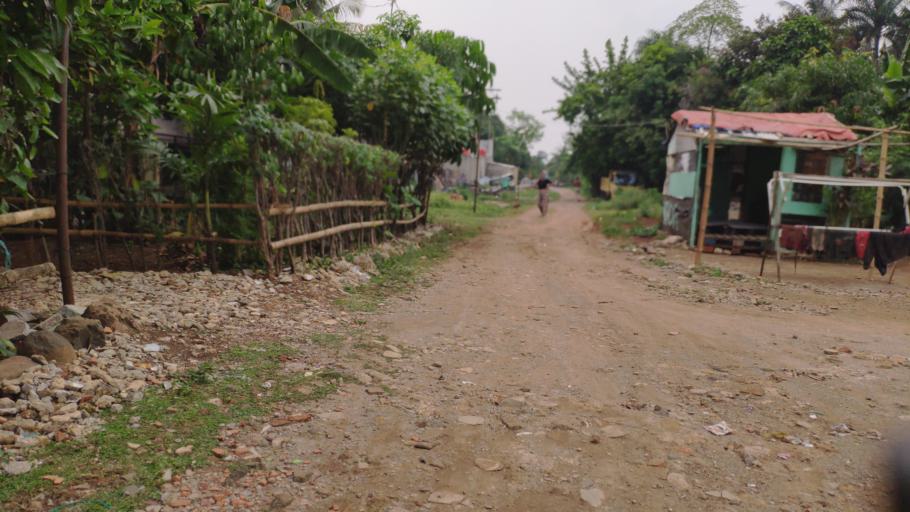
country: ID
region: West Java
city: Depok
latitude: -6.3675
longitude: 106.8069
